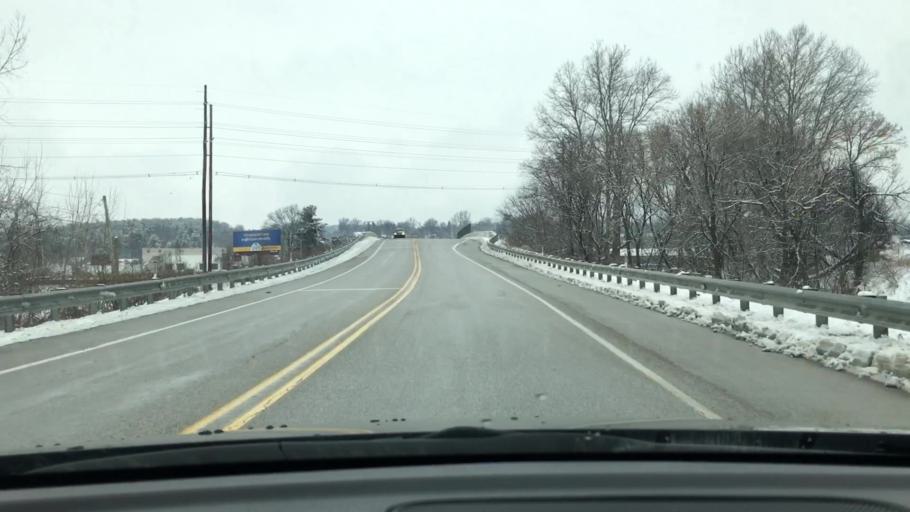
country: US
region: Pennsylvania
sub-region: York County
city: North York
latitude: 39.9778
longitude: -76.7103
